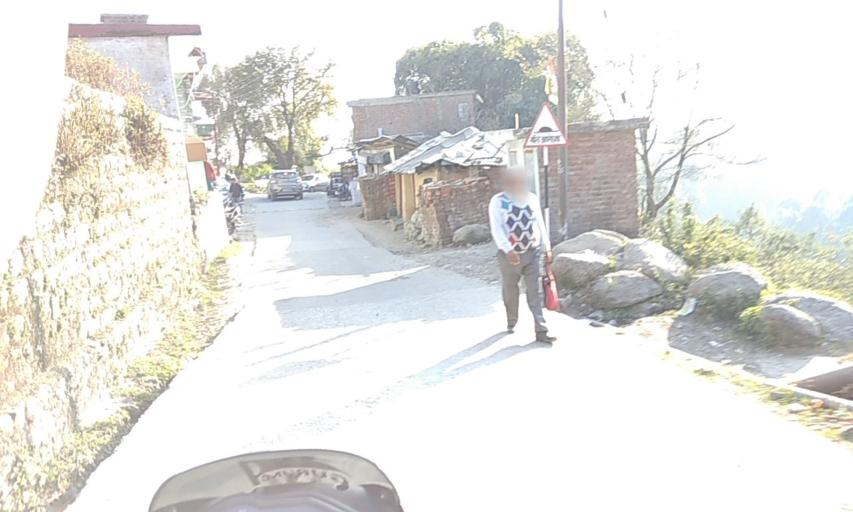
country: IN
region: Himachal Pradesh
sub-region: Kangra
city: Palampur
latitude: 32.1304
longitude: 76.5359
